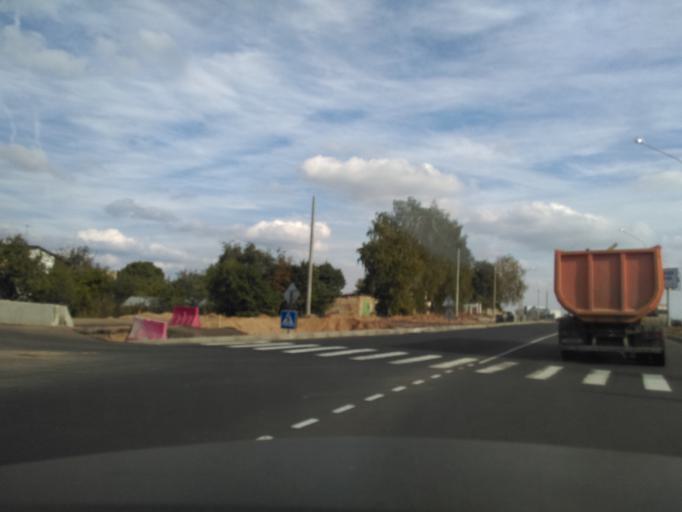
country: BY
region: Minsk
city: Machulishchy
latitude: 53.8363
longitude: 27.5994
